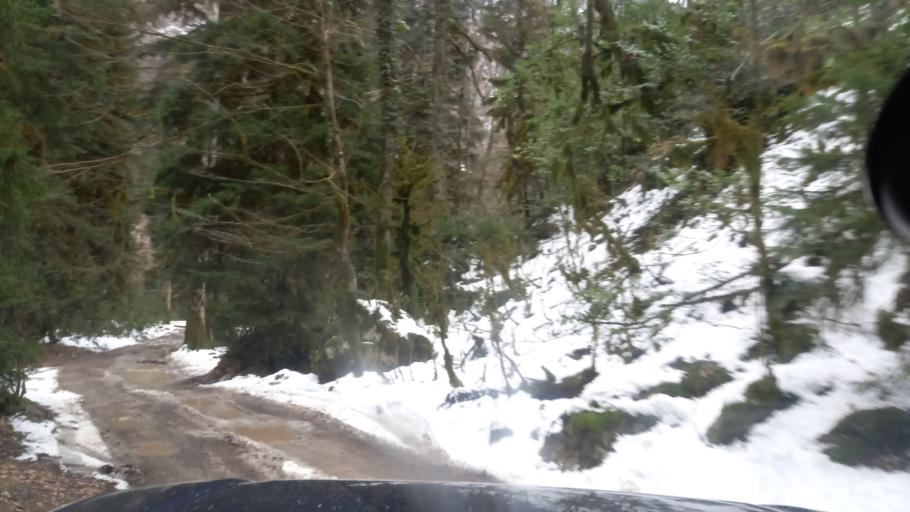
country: GE
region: Abkhazia
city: Gagra
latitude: 43.4329
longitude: 40.4449
